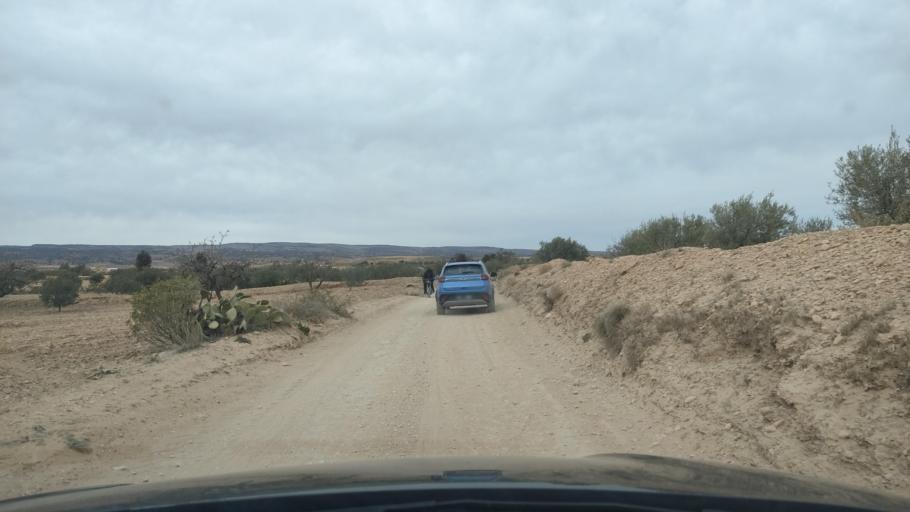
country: TN
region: Al Qasrayn
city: Kasserine
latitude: 35.2540
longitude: 8.9217
